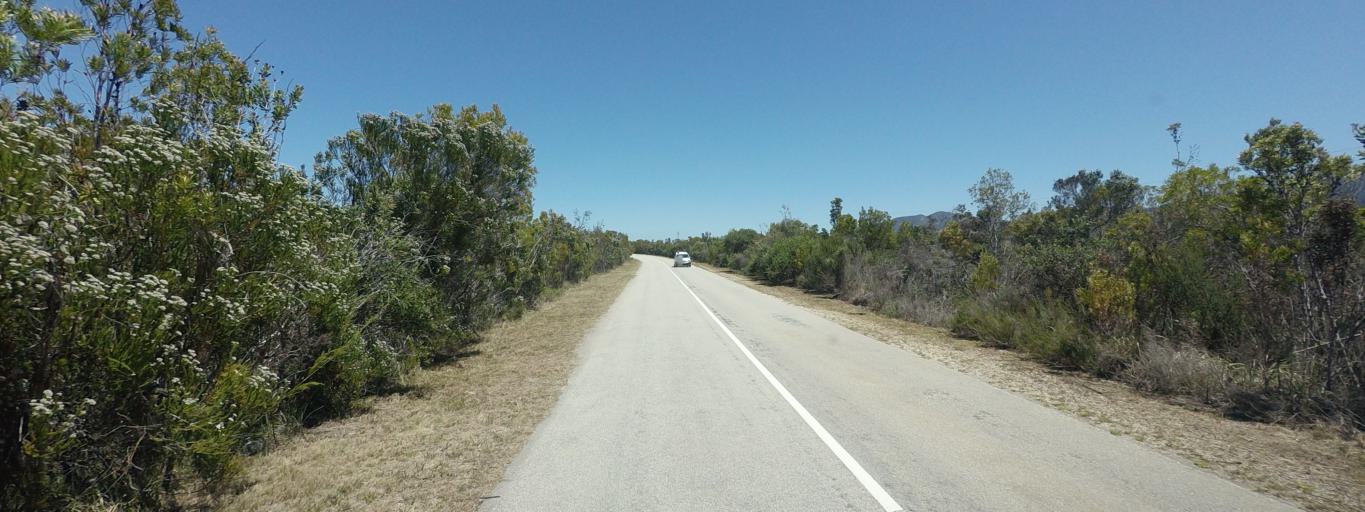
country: ZA
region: Western Cape
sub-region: Eden District Municipality
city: Plettenberg Bay
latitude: -33.9603
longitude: 23.5379
